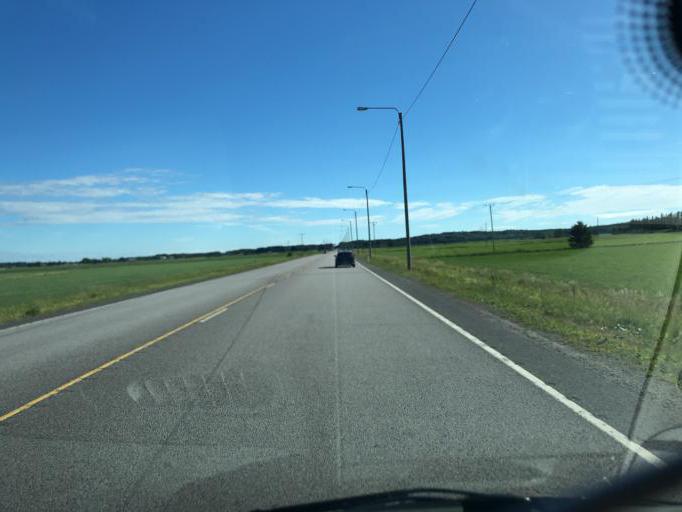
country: FI
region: Uusimaa
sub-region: Loviisa
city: Lapinjaervi
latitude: 60.6618
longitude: 26.2445
